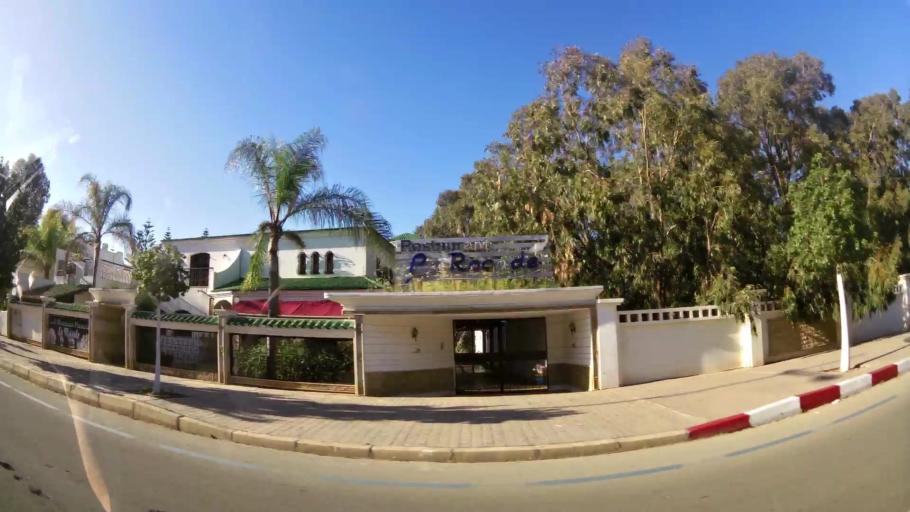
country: MA
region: Oriental
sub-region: Berkane-Taourirt
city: Madagh
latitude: 35.0909
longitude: -2.2522
